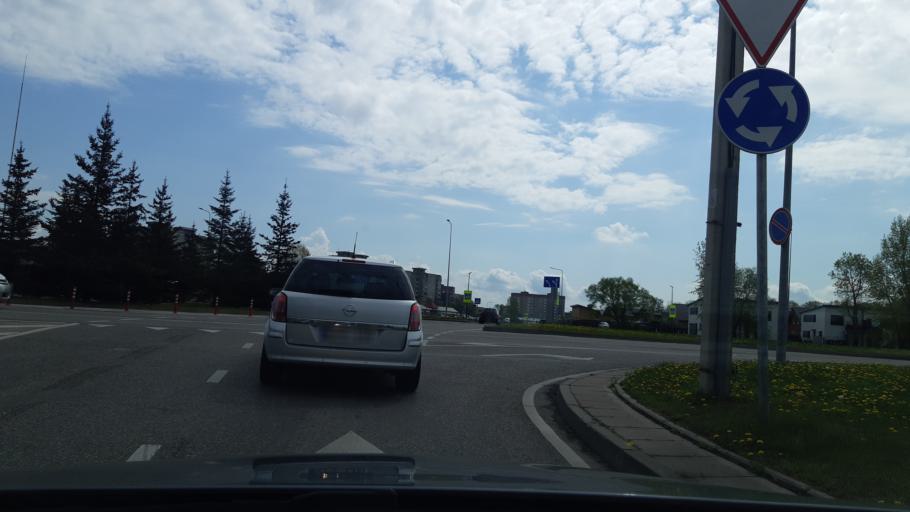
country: LT
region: Kauno apskritis
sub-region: Kaunas
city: Silainiai
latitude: 54.9228
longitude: 23.8689
